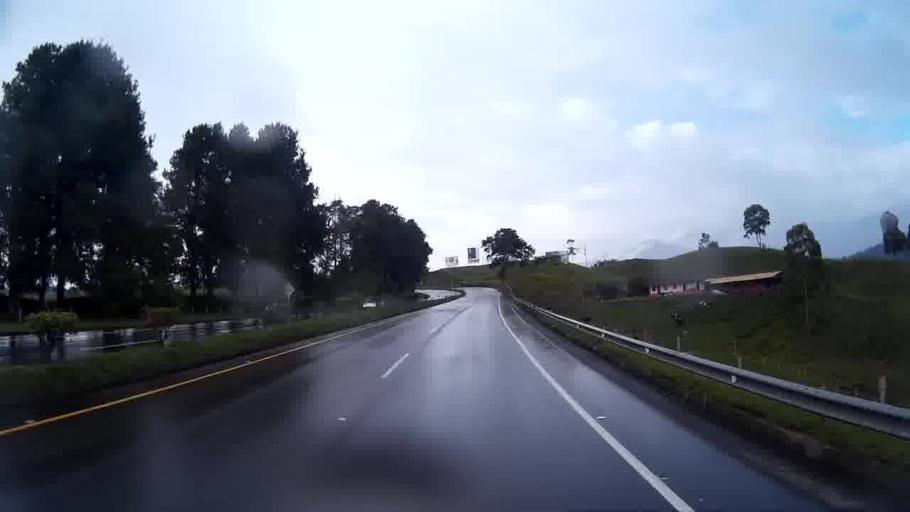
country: CO
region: Quindio
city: Salento
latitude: 4.6668
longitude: -75.5958
